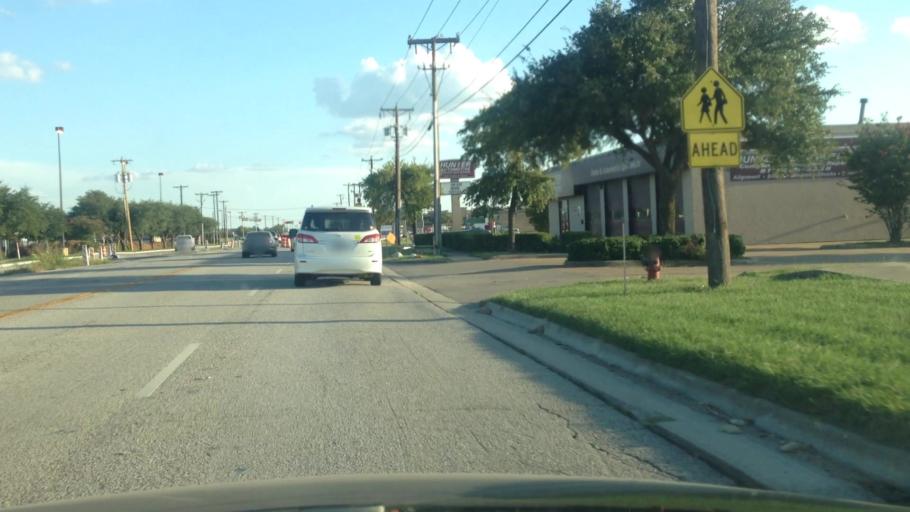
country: US
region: Texas
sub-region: Tarrant County
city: Watauga
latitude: 32.8772
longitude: -97.2380
